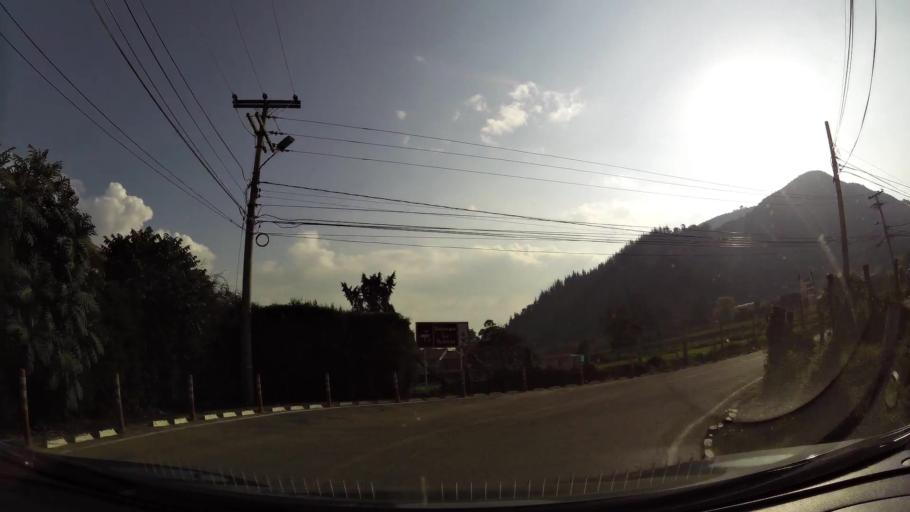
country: CO
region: Cundinamarca
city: Cota
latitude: 4.8053
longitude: -74.1115
